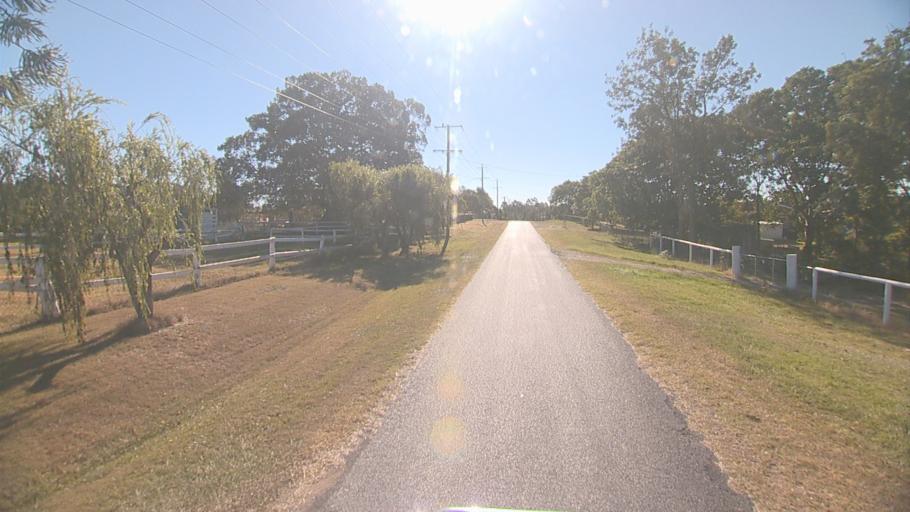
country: AU
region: Queensland
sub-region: Logan
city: North Maclean
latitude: -27.7843
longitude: 153.0196
